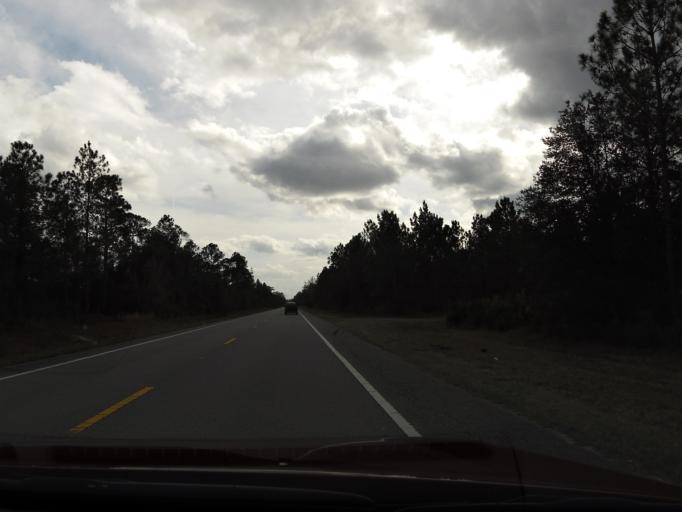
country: US
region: Florida
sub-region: Volusia County
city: De Leon Springs
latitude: 29.2497
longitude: -81.3260
